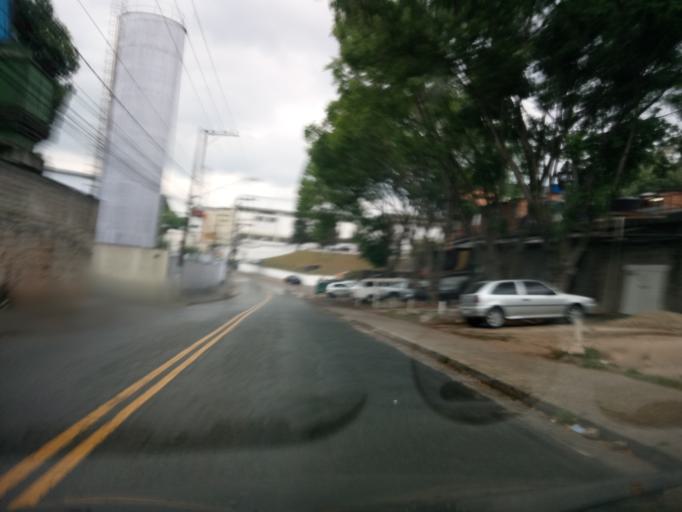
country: BR
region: Sao Paulo
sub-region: Sao Bernardo Do Campo
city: Sao Bernardo do Campo
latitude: -23.7274
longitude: -46.5902
